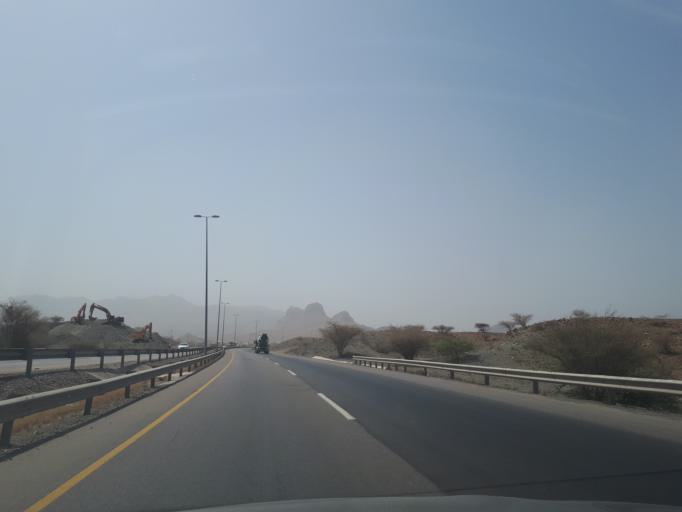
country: OM
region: Muhafazat ad Dakhiliyah
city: Bidbid
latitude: 23.5052
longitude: 58.1928
